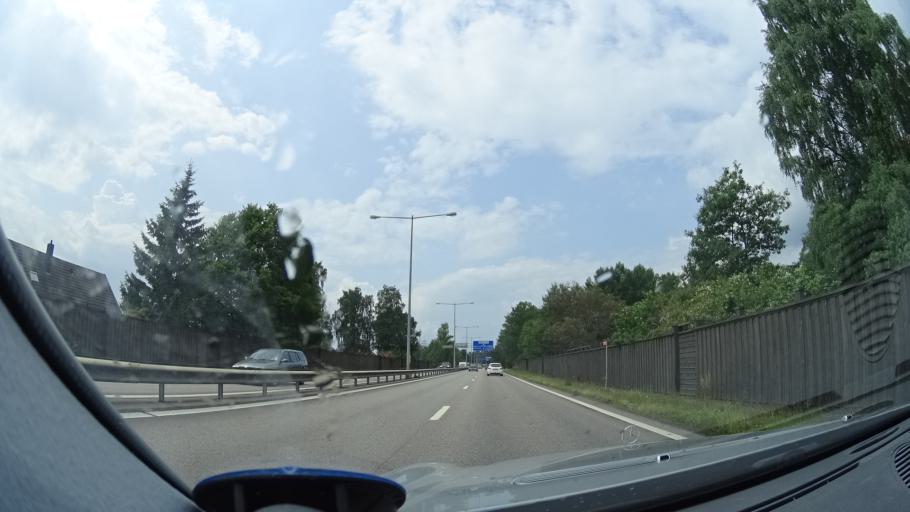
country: SE
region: Kalmar
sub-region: Nybro Kommun
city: Nybro
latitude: 56.7340
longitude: 15.9413
